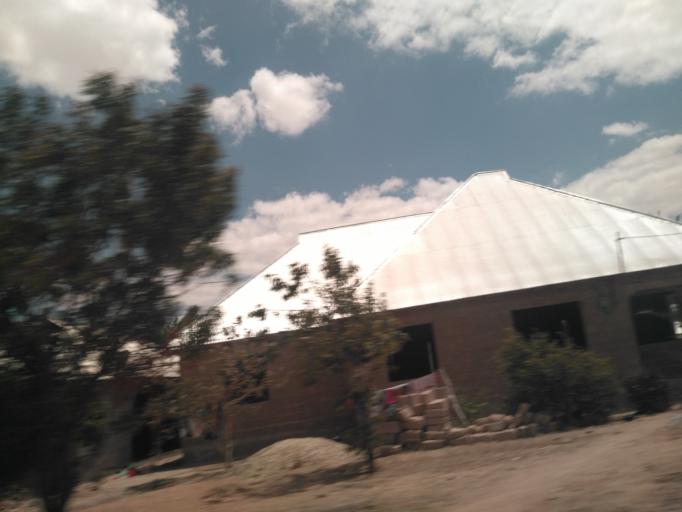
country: TZ
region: Dodoma
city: Kisasa
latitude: -6.1697
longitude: 35.7959
